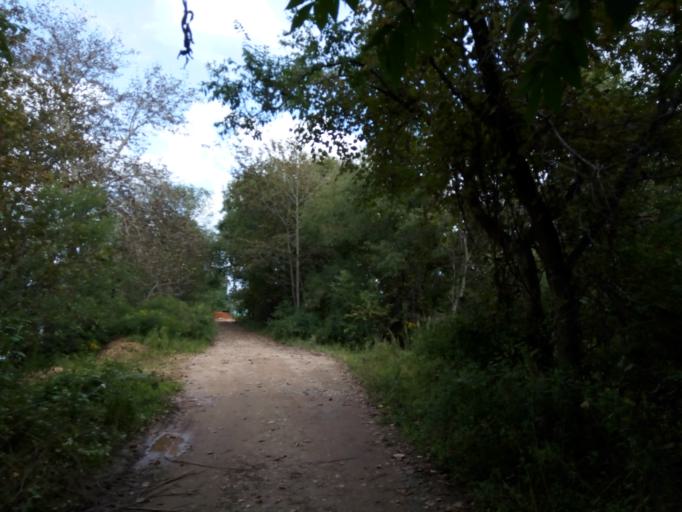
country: RU
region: Primorskiy
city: Dal'nerechensk
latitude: 45.9540
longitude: 133.8124
